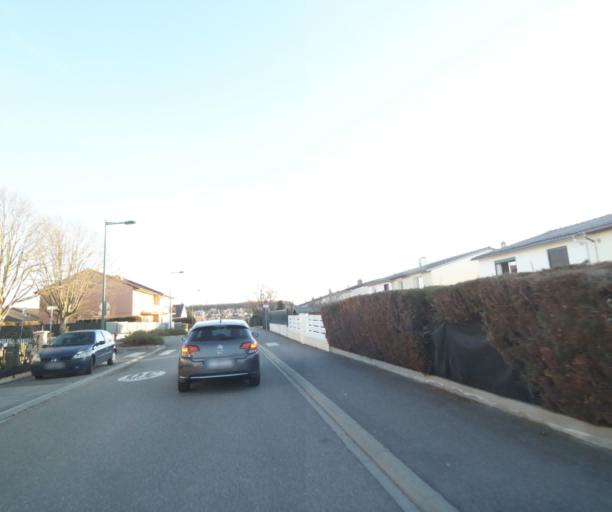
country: FR
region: Lorraine
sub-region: Departement de Meurthe-et-Moselle
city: Saulxures-les-Nancy
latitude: 48.6857
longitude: 6.2358
